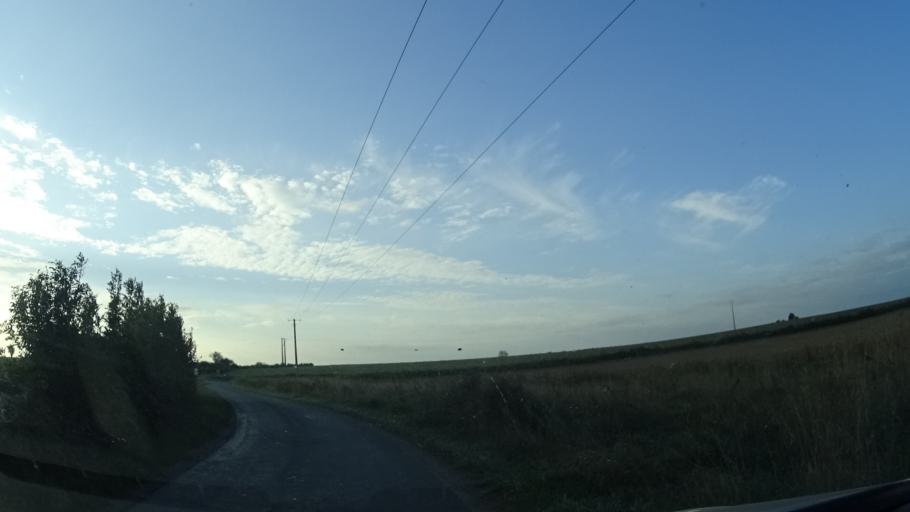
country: BE
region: Wallonia
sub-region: Province du Hainaut
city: Beaumont
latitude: 50.2418
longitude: 4.2670
